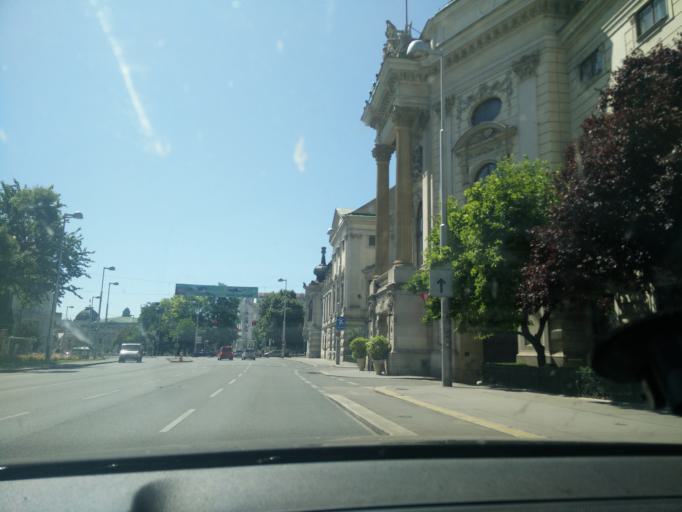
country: AT
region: Vienna
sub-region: Wien Stadt
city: Vienna
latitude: 48.2078
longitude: 16.3553
